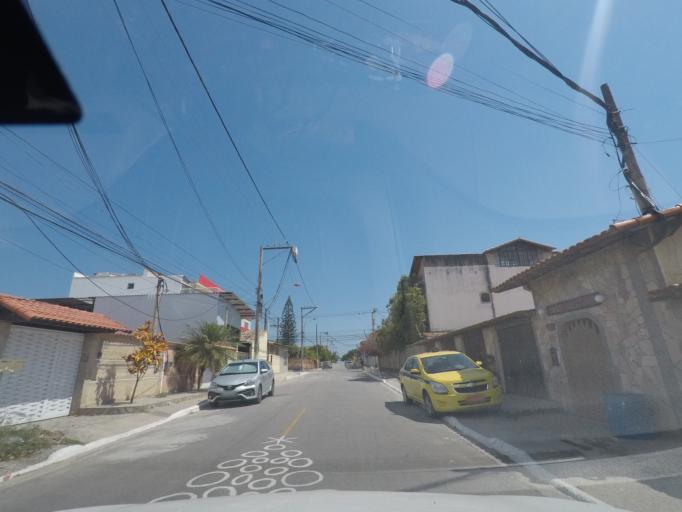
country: BR
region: Rio de Janeiro
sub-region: Marica
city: Marica
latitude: -22.9641
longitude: -42.9631
